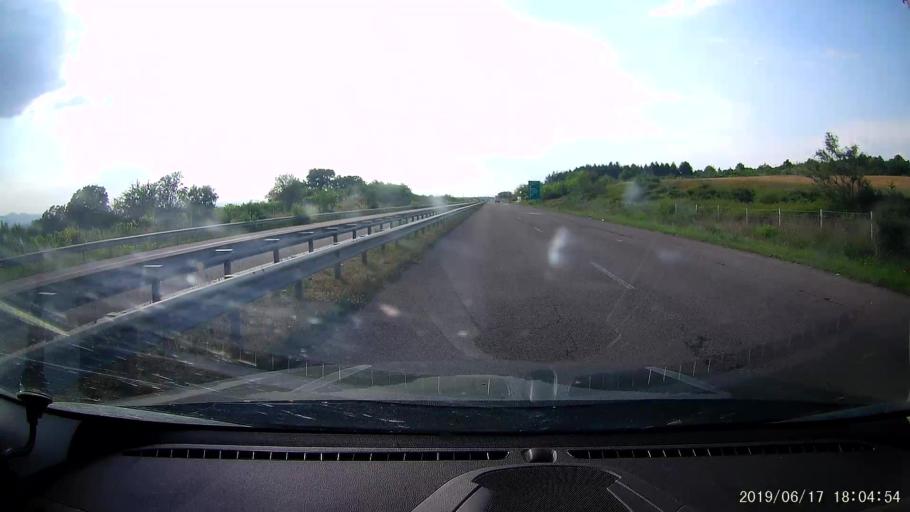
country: BG
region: Khaskovo
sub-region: Obshtina Svilengrad
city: Svilengrad
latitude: 41.7914
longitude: 26.1879
